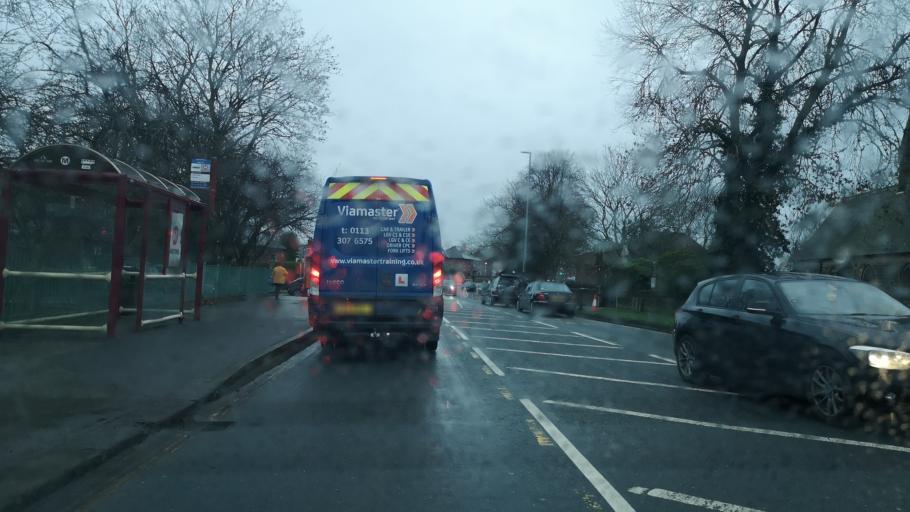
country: GB
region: England
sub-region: City and Borough of Wakefield
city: Sharlston
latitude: 53.6671
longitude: -1.4162
